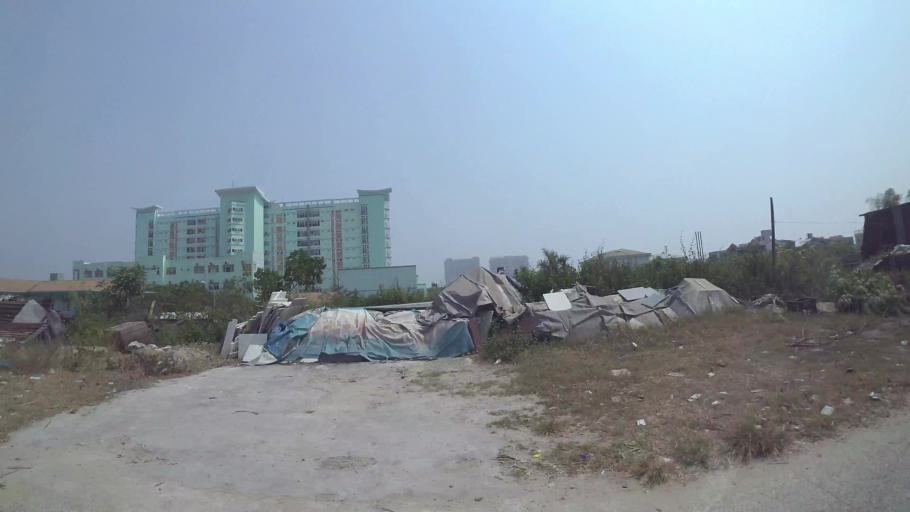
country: VN
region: Da Nang
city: Ngu Hanh Son
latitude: 16.0219
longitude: 108.2482
